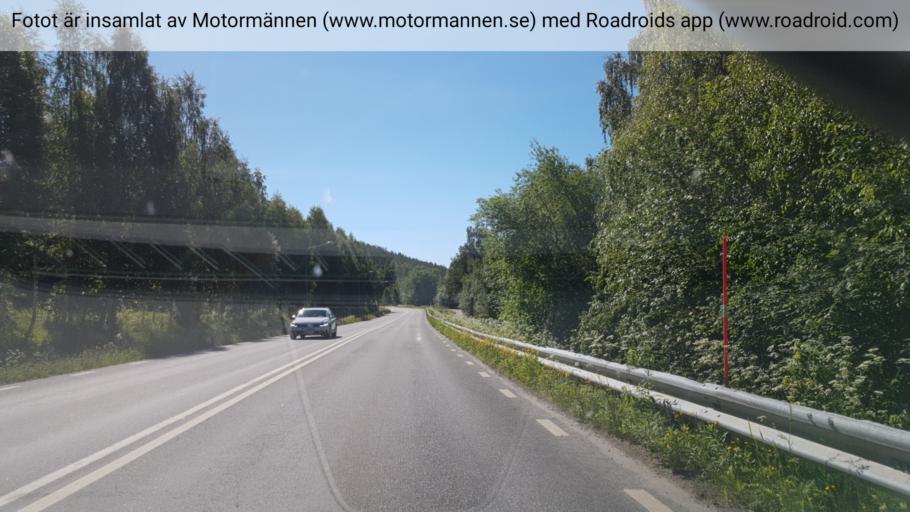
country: SE
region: Norrbotten
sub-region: Bodens Kommun
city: Boden
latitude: 65.8406
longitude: 21.6070
